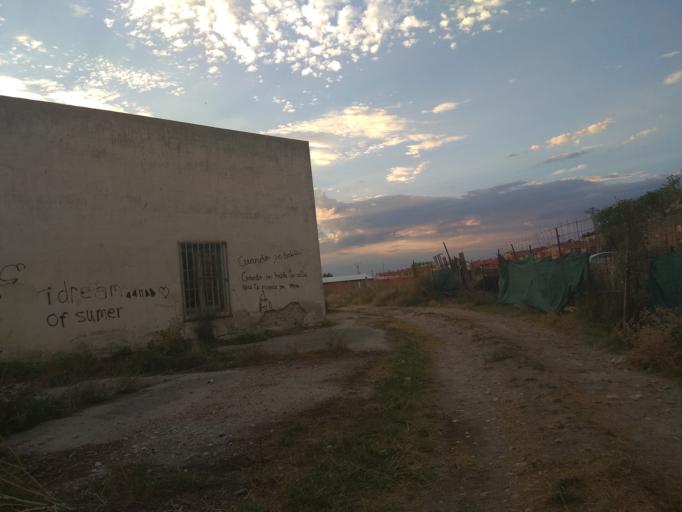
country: ES
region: Castille and Leon
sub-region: Provincia de Valladolid
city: Portillo
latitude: 41.4711
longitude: -4.5940
